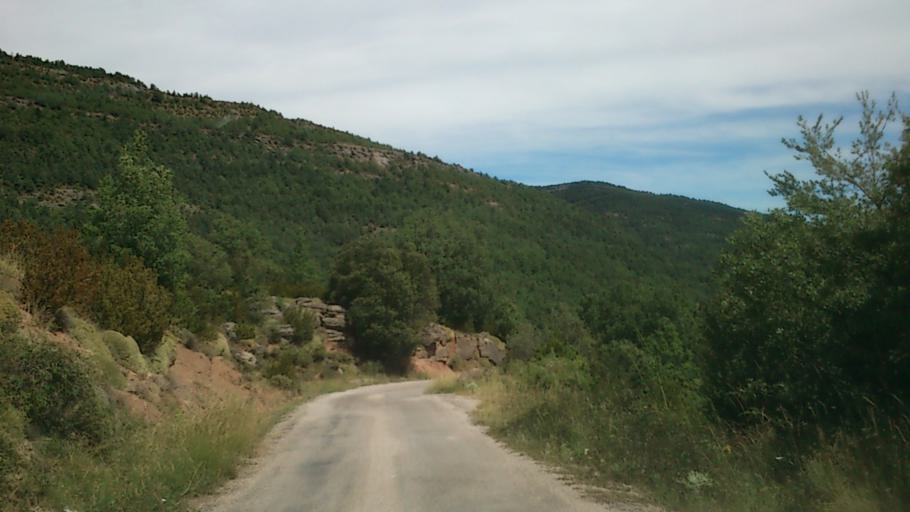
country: ES
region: Aragon
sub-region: Provincia de Huesca
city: Loporzano
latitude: 42.3189
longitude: -0.2669
